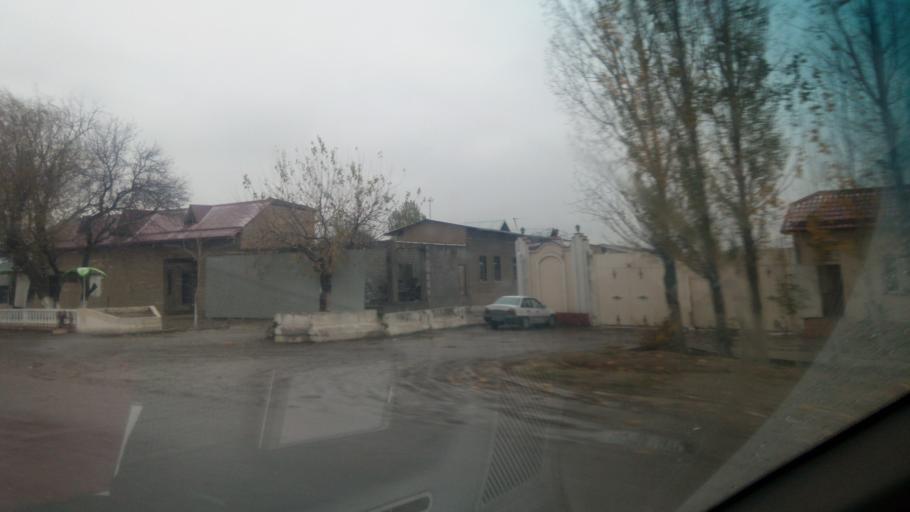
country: UZ
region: Toshkent
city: Urtaowul
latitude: 41.2267
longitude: 69.1458
